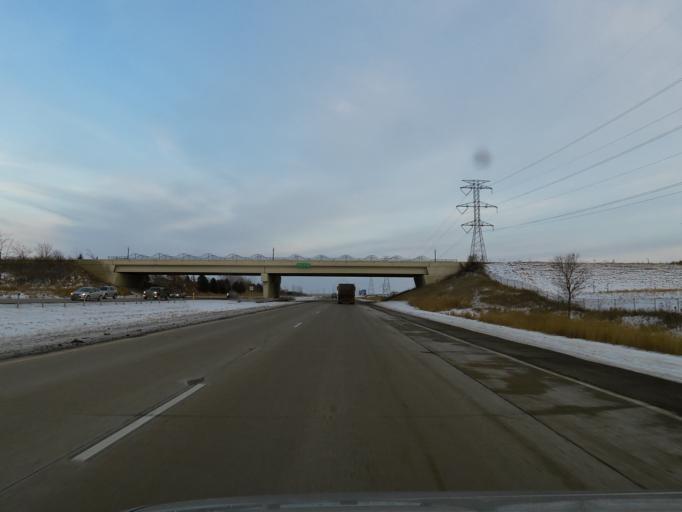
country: US
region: Minnesota
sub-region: Scott County
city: Shakopee
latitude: 44.7761
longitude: -93.5321
